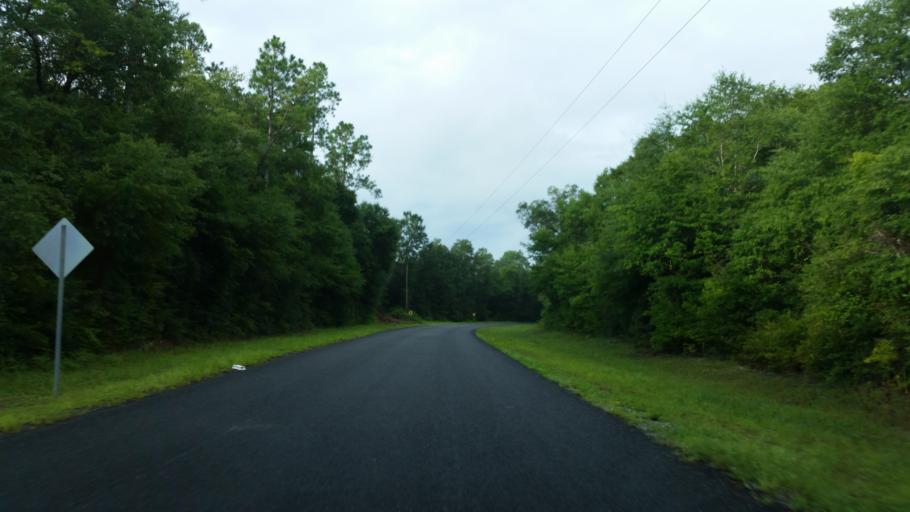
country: US
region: Florida
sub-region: Okaloosa County
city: Crestview
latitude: 30.6772
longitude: -86.7494
